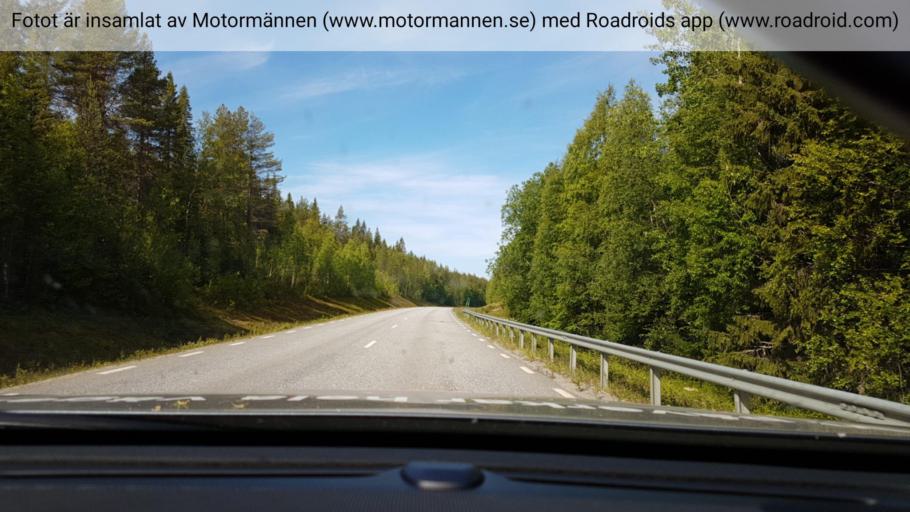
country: SE
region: Vaesterbotten
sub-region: Dorotea Kommun
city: Dorotea
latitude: 64.2373
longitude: 16.7656
